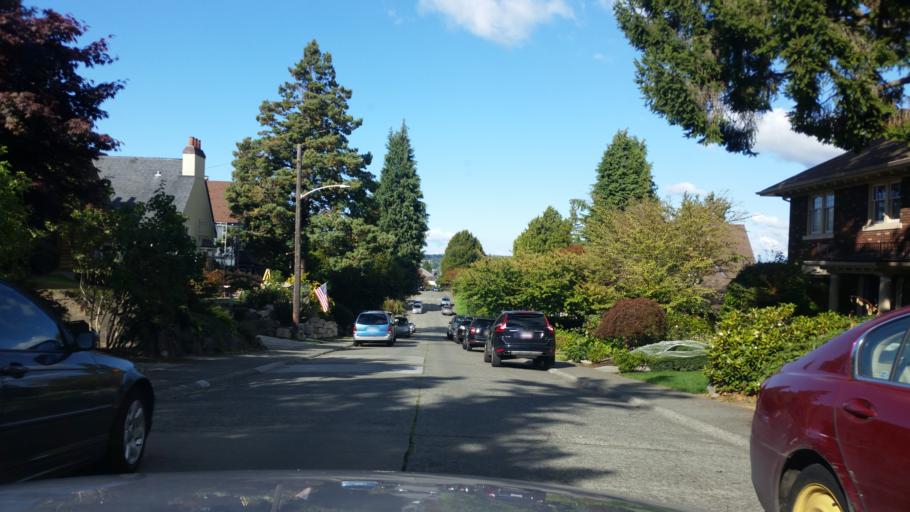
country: US
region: Washington
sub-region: King County
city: Seattle
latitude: 47.6474
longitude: -122.3705
